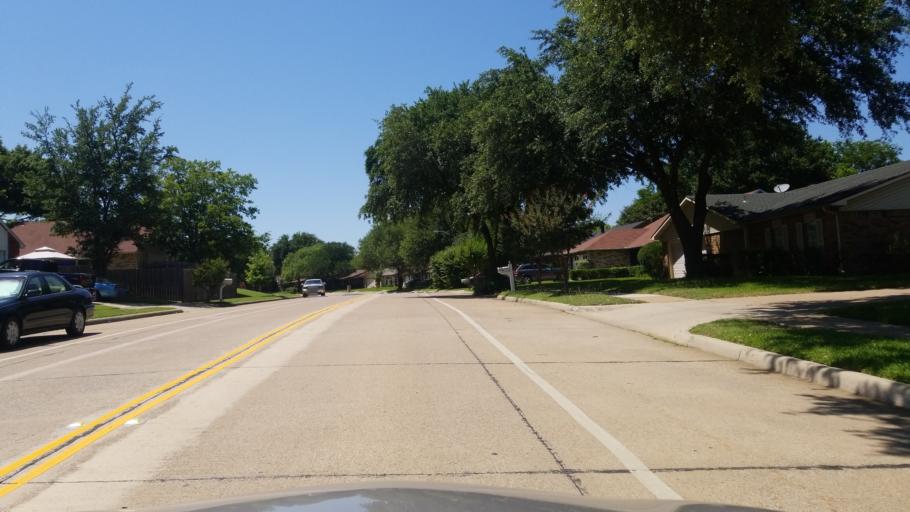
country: US
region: Texas
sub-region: Dallas County
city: Grand Prairie
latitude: 32.6795
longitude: -97.0044
